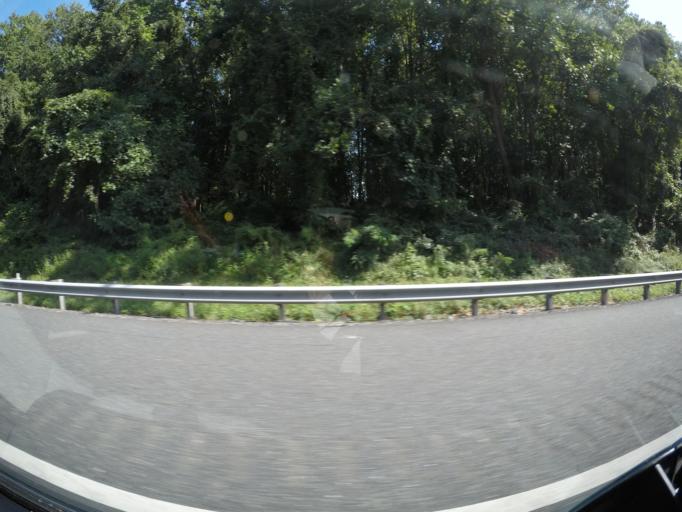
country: US
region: Maryland
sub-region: Harford County
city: Joppatowne
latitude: 39.4340
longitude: -76.3799
